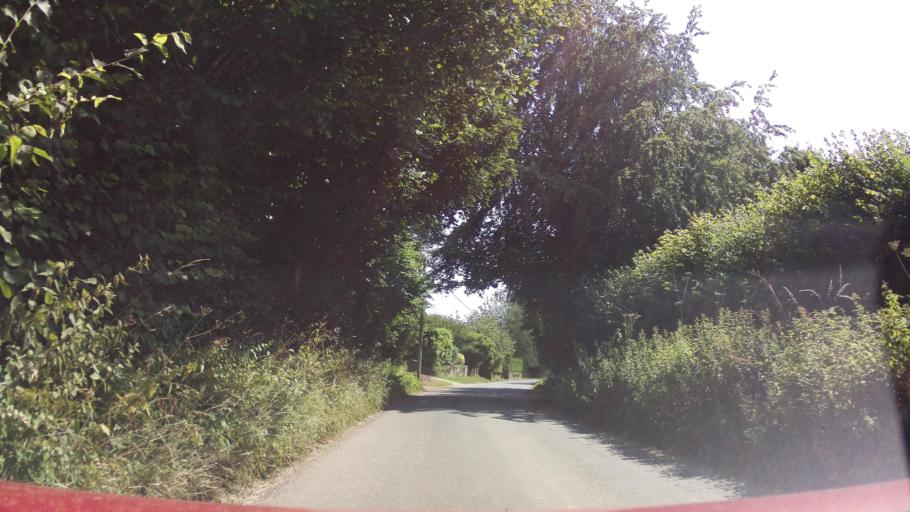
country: GB
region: England
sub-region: Wiltshire
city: Hankerton
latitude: 51.6332
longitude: -2.0396
